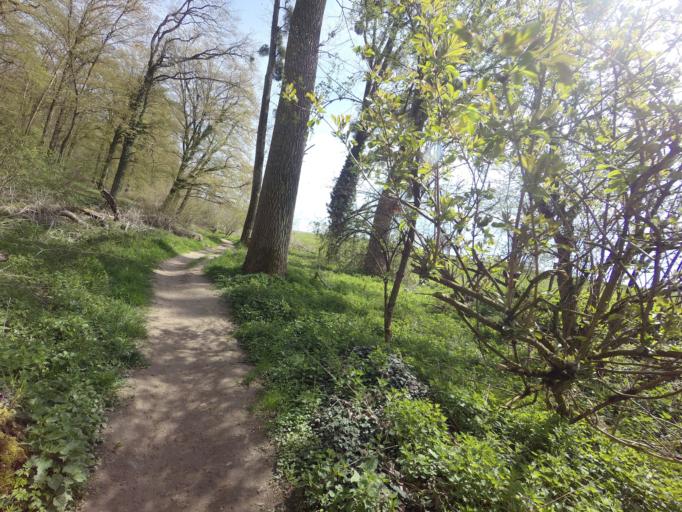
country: NL
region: Limburg
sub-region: Eijsden-Margraten
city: Eijsden
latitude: 50.7738
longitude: 5.7721
